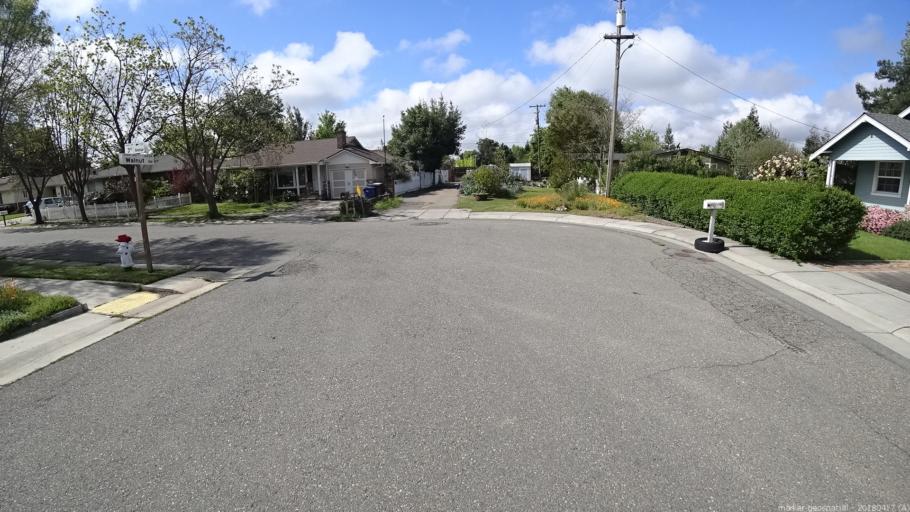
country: US
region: California
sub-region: Sacramento County
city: Walnut Grove
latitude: 38.2465
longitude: -121.5161
